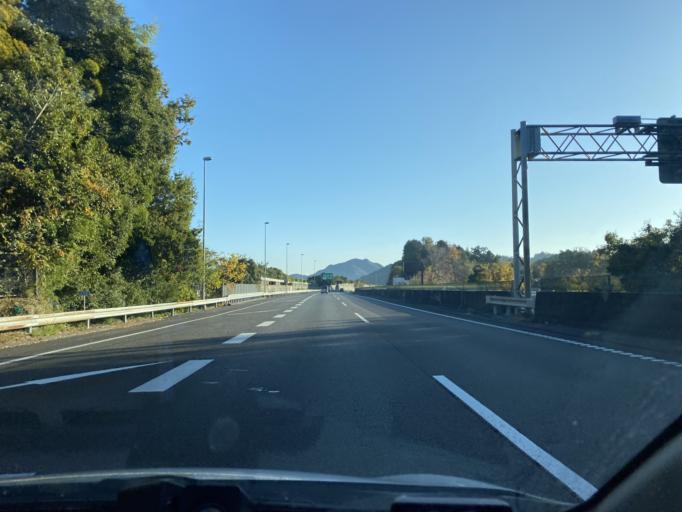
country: JP
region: Shiga Prefecture
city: Kusatsu
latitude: 35.0207
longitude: 136.0102
